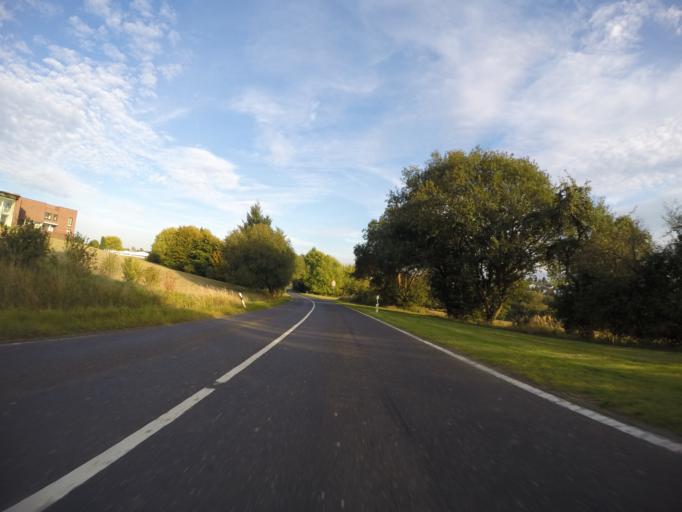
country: DE
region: Rheinland-Pfalz
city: Grossmaischeid
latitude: 50.5066
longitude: 7.6284
